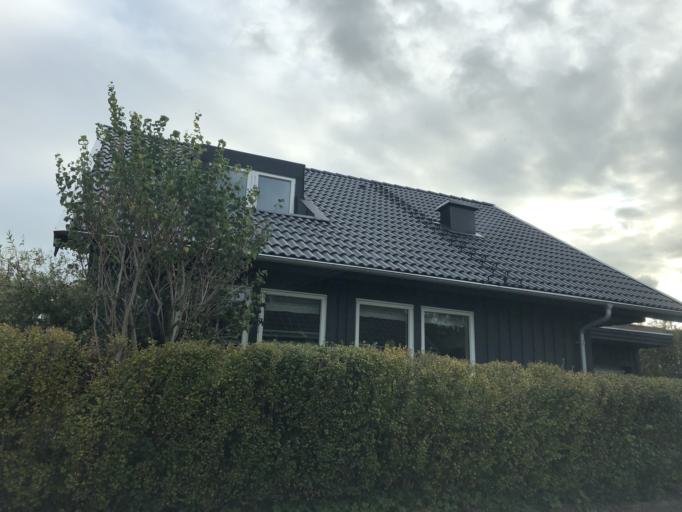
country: SE
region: Vaestra Goetaland
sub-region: Goteborg
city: Majorna
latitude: 57.6790
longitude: 11.8731
